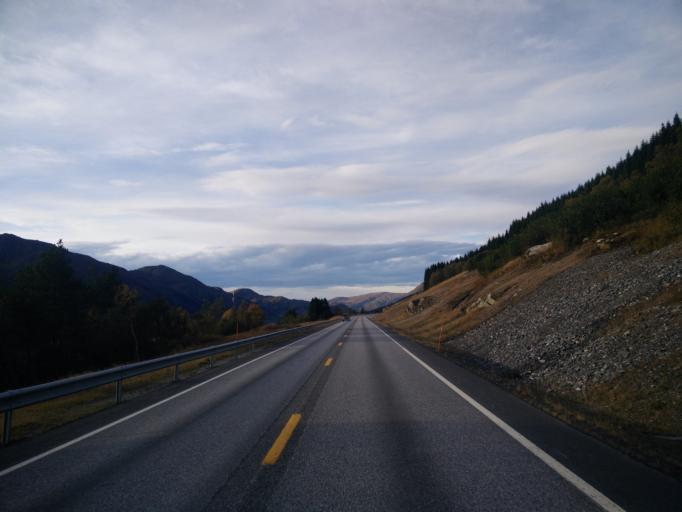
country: NO
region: More og Romsdal
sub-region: Gjemnes
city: Batnfjordsora
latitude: 62.9339
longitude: 7.7287
